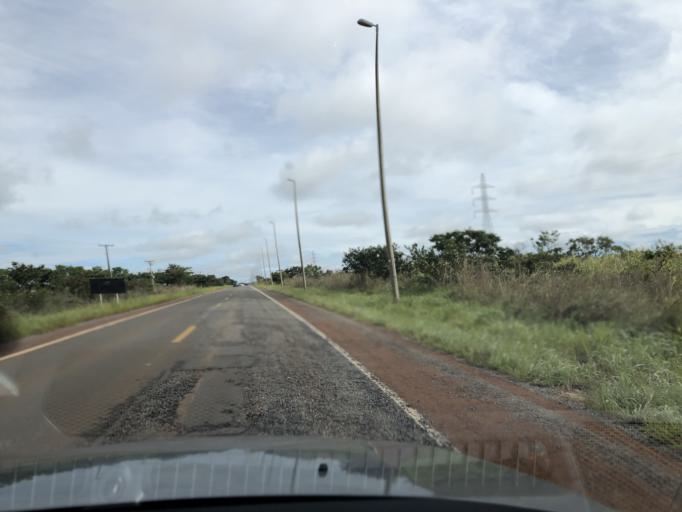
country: BR
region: Federal District
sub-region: Brasilia
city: Brasilia
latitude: -15.7031
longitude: -48.0880
